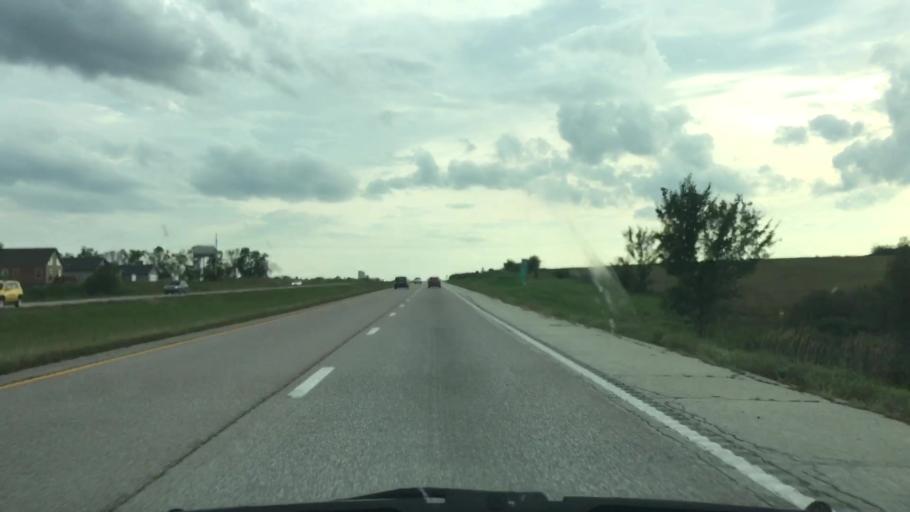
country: US
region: Missouri
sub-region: Clinton County
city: Lathrop
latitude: 39.5383
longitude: -94.2754
